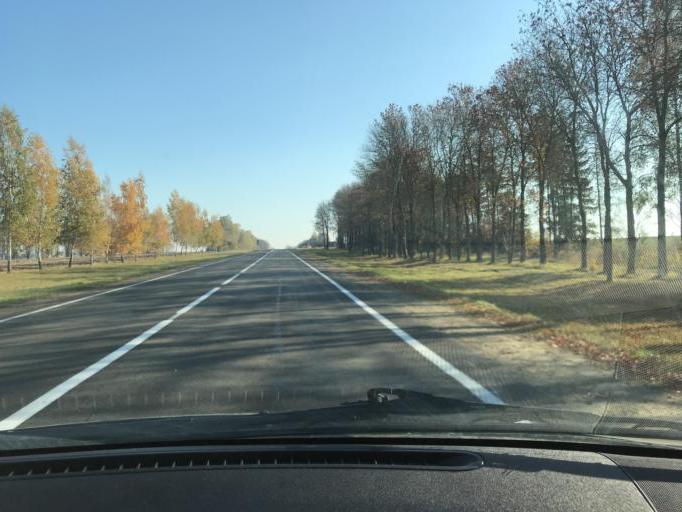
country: BY
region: Minsk
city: Klyetsk
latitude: 52.9638
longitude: 26.4876
